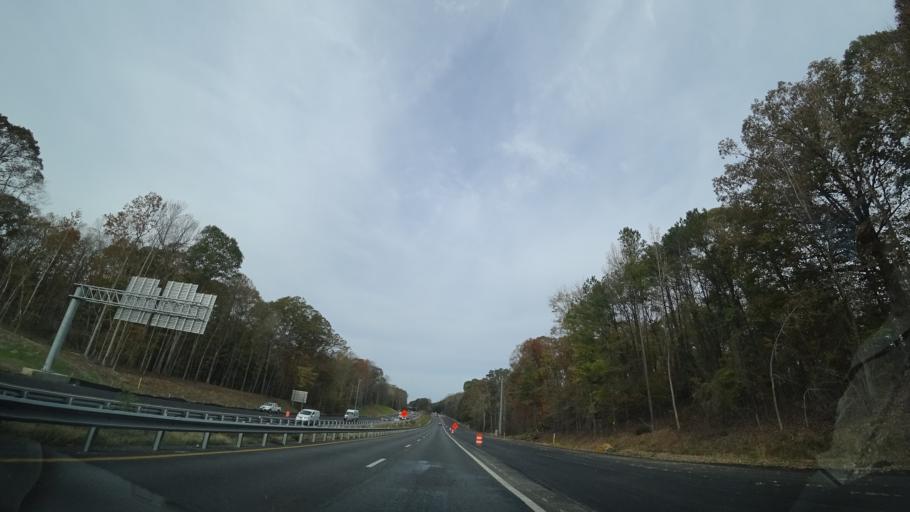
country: US
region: Virginia
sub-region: City of Williamsburg
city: Williamsburg
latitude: 37.2663
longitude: -76.6522
